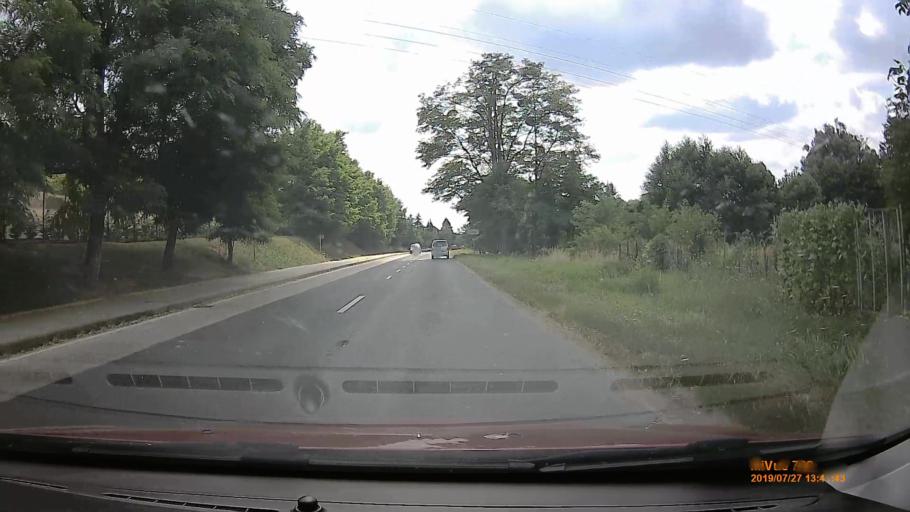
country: HU
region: Veszprem
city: Ajka
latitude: 47.1198
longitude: 17.5652
